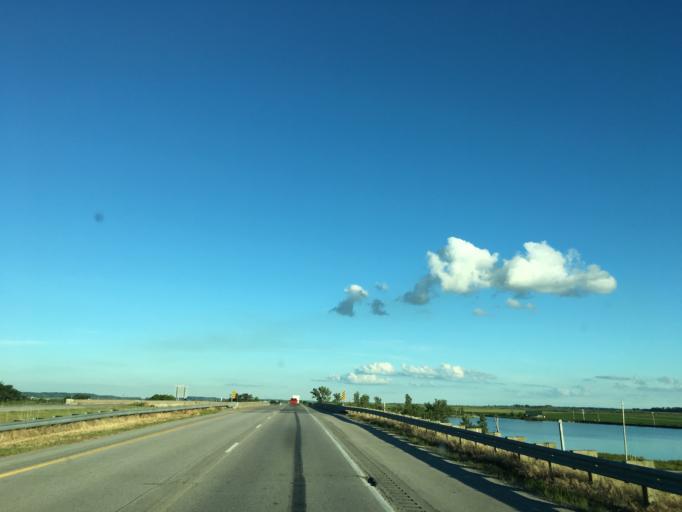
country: US
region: Nebraska
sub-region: Otoe County
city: Nebraska City
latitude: 40.6703
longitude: -95.7669
